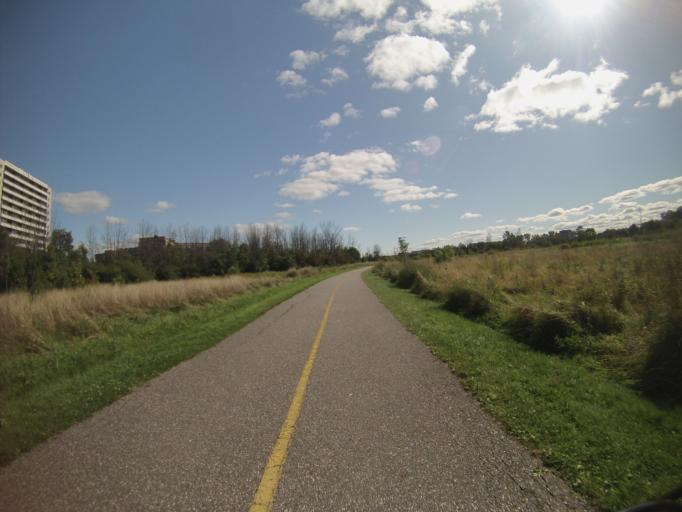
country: CA
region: Ontario
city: Bells Corners
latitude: 45.3562
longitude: -75.7593
